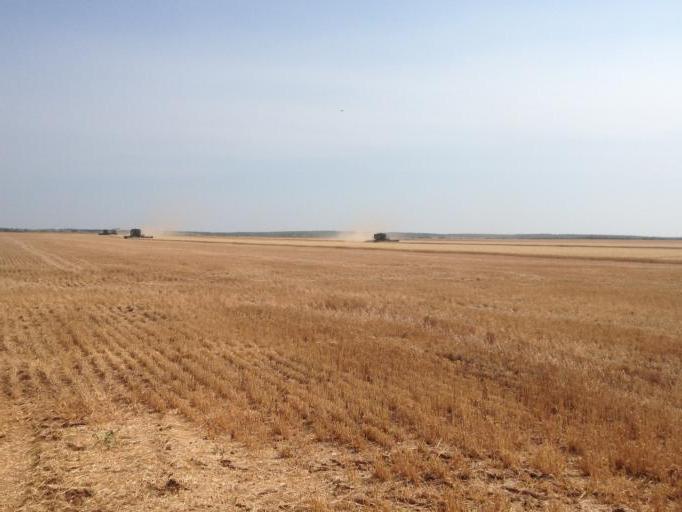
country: US
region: Texas
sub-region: Childress County
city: Childress
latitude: 34.4362
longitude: -100.0410
